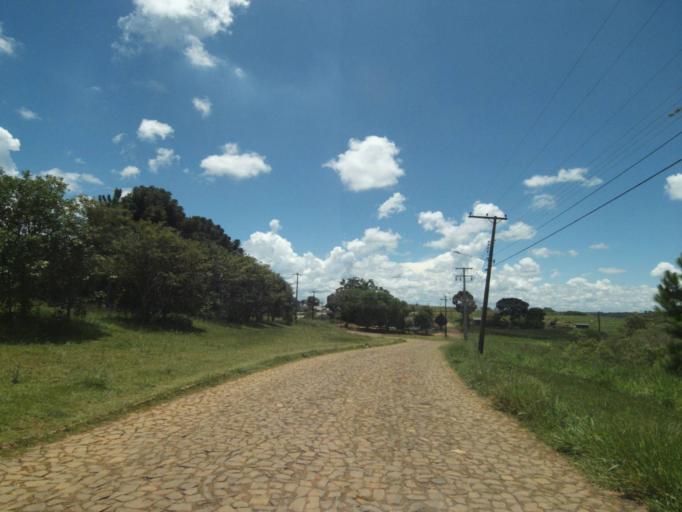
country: BR
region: Parana
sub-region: Pinhao
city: Pinhao
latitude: -25.7908
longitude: -52.0813
